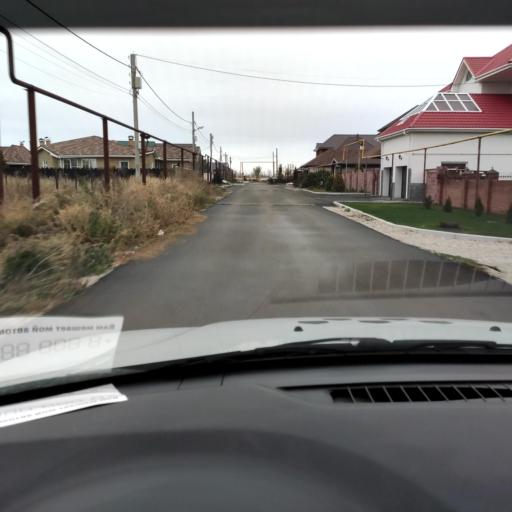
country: RU
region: Samara
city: Podstepki
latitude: 53.5135
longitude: 49.2080
